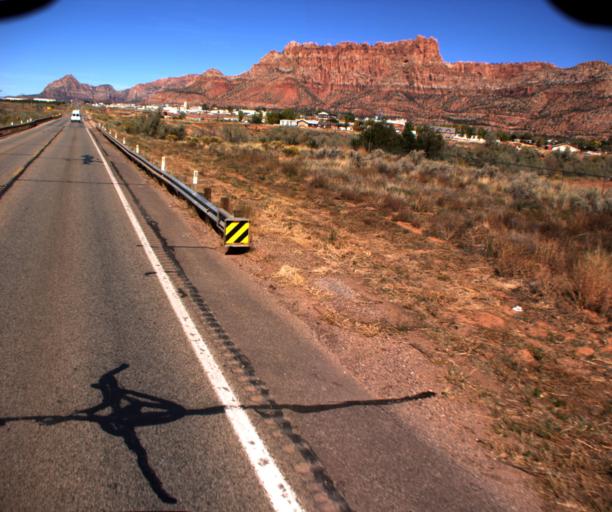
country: US
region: Arizona
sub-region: Mohave County
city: Colorado City
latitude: 36.9870
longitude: -112.9882
